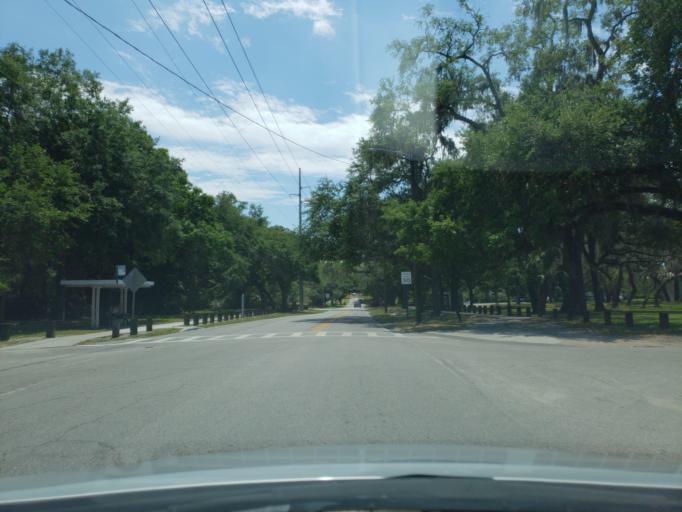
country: US
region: Florida
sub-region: Hillsborough County
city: Egypt Lake-Leto
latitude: 28.0151
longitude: -82.4678
